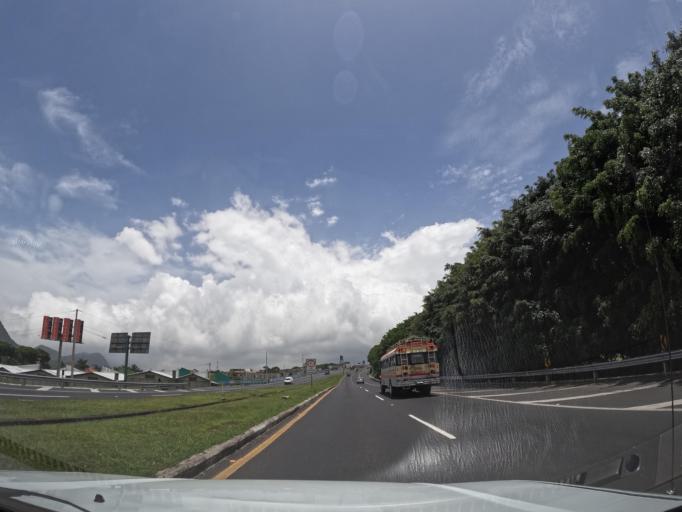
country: GT
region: Escuintla
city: Palin
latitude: 14.4108
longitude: -90.6836
